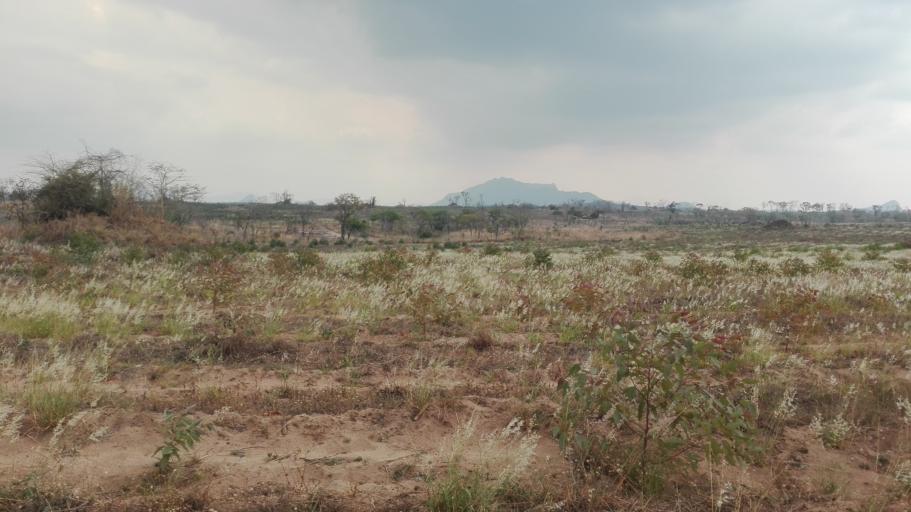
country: MZ
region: Nampula
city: Mutuali
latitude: -15.6861
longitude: 36.8895
